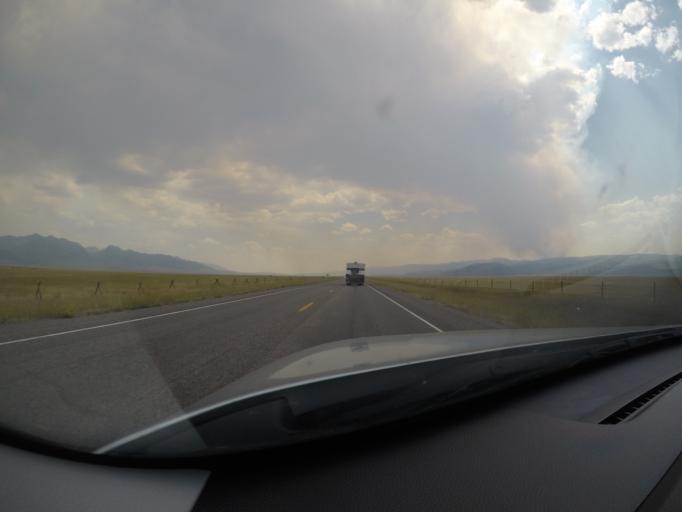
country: US
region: Montana
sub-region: Madison County
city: Virginia City
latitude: 45.1508
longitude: -111.6787
